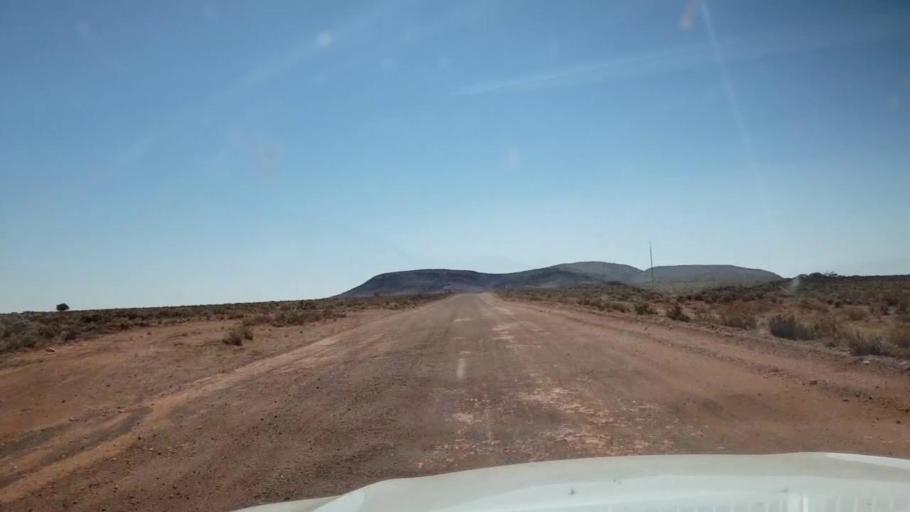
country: AU
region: South Australia
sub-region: Whyalla
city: Whyalla
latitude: -32.7075
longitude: 137.1383
